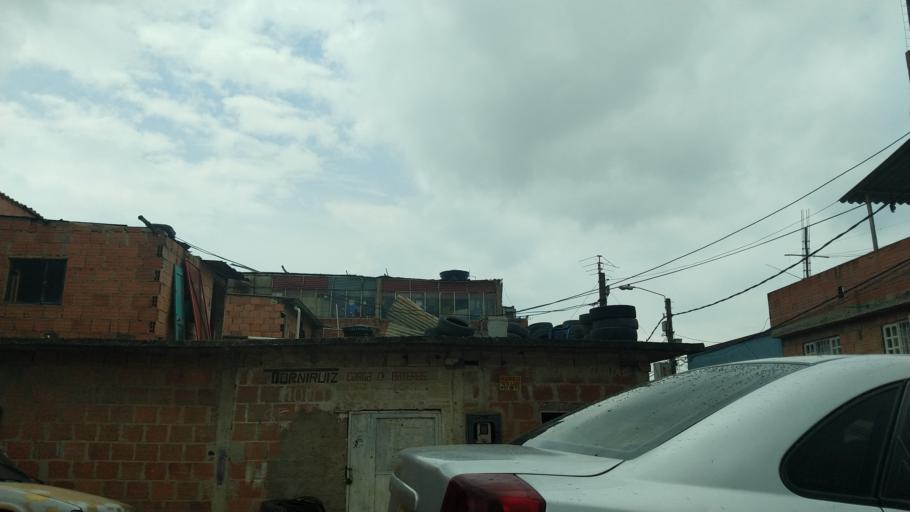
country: CO
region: Cundinamarca
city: Soacha
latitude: 4.5659
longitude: -74.1879
